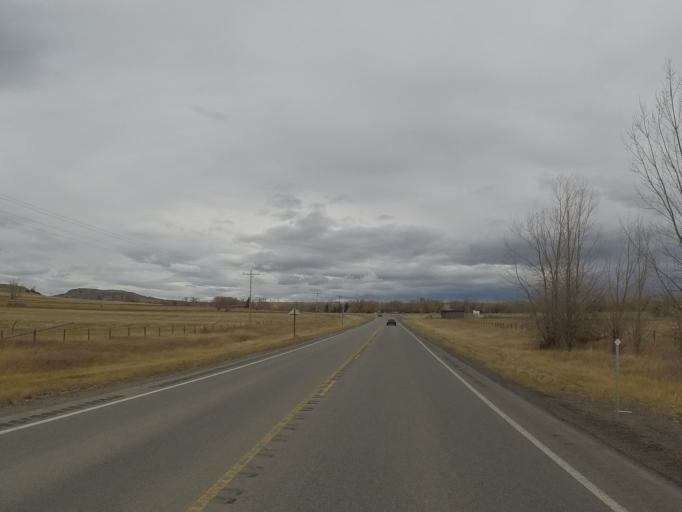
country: US
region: Montana
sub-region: Sweet Grass County
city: Big Timber
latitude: 45.8492
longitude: -109.9407
